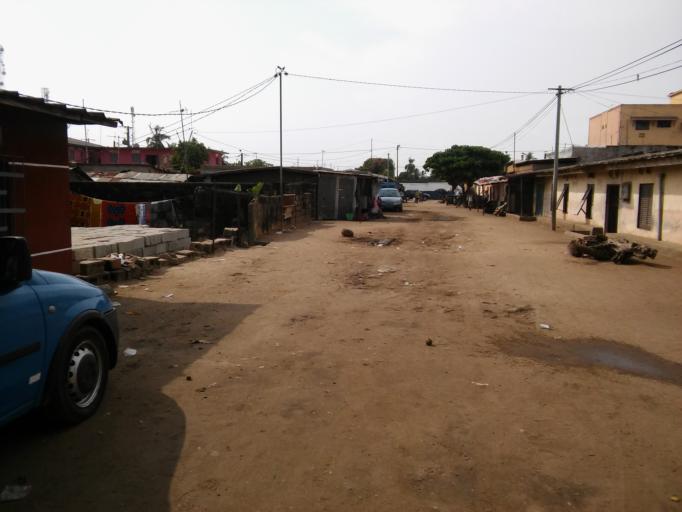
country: CI
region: Sud-Comoe
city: Grand-Bassam
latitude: 5.2072
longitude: -3.7341
